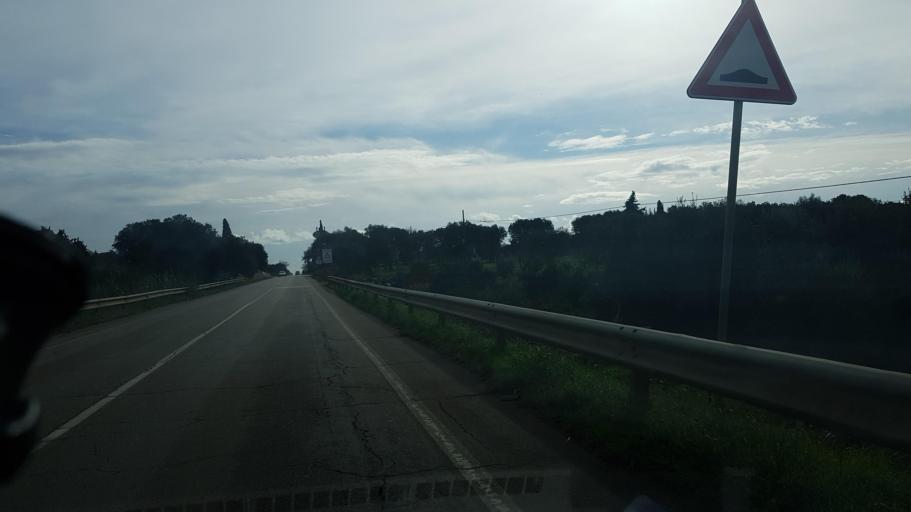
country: IT
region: Apulia
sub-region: Provincia di Brindisi
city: San Vito dei Normanni
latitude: 40.6808
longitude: 17.6838
